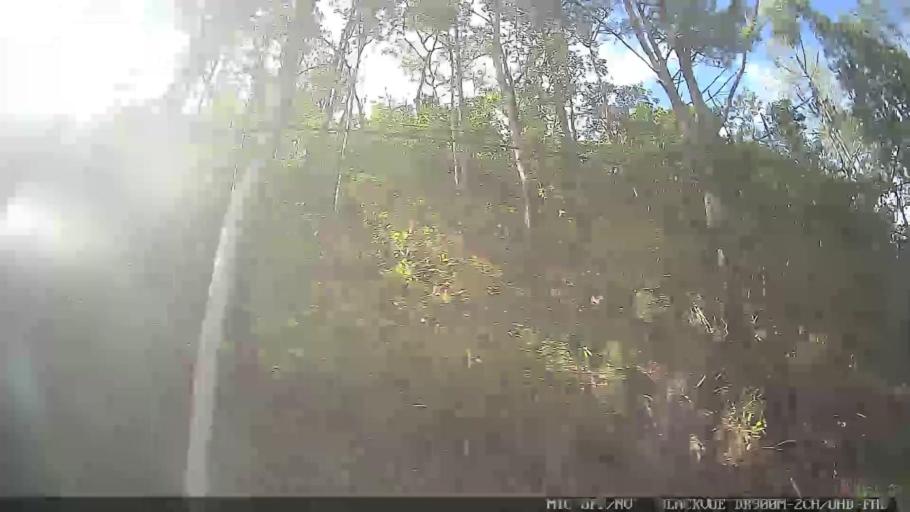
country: BR
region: Sao Paulo
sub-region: Serra Negra
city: Serra Negra
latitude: -22.6065
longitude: -46.7280
